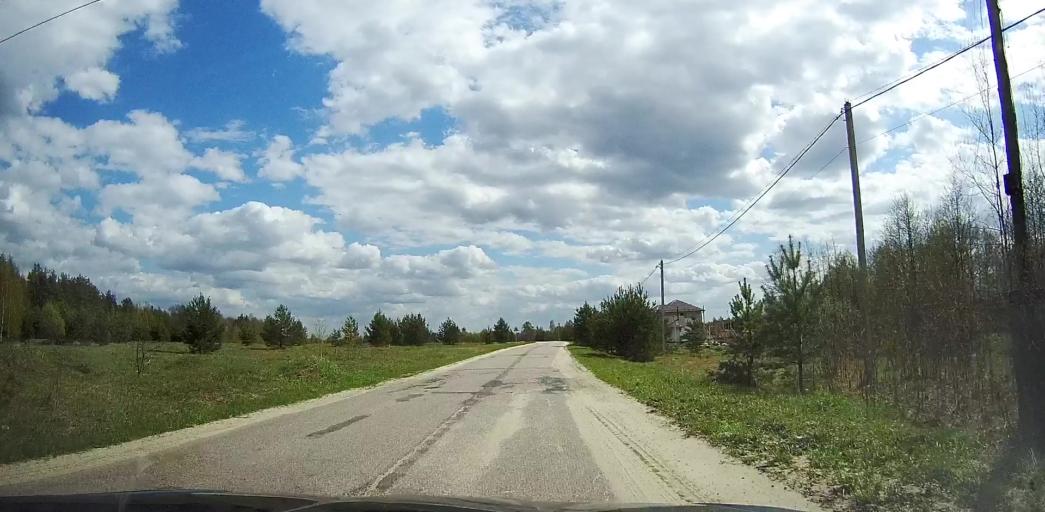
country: RU
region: Moskovskaya
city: Davydovo
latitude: 55.6435
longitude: 38.7741
